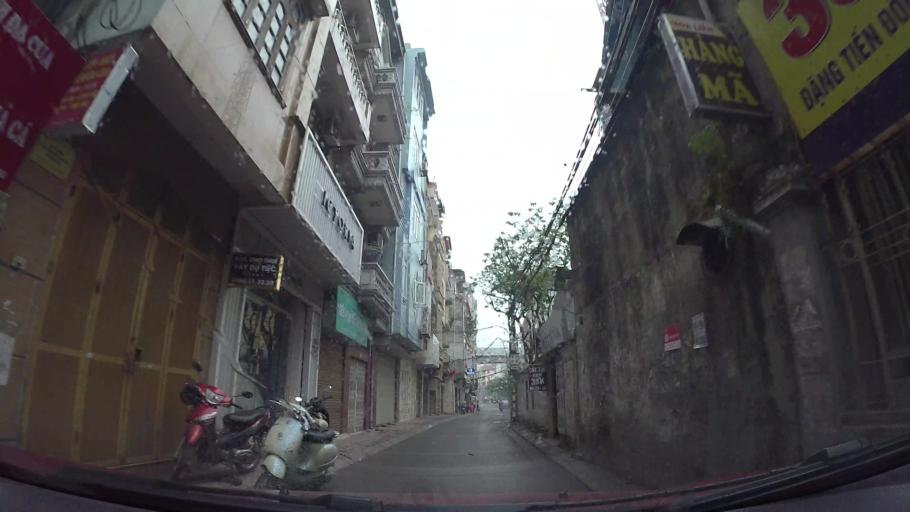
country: VN
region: Ha Noi
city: Dong Da
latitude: 21.0147
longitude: 105.8211
